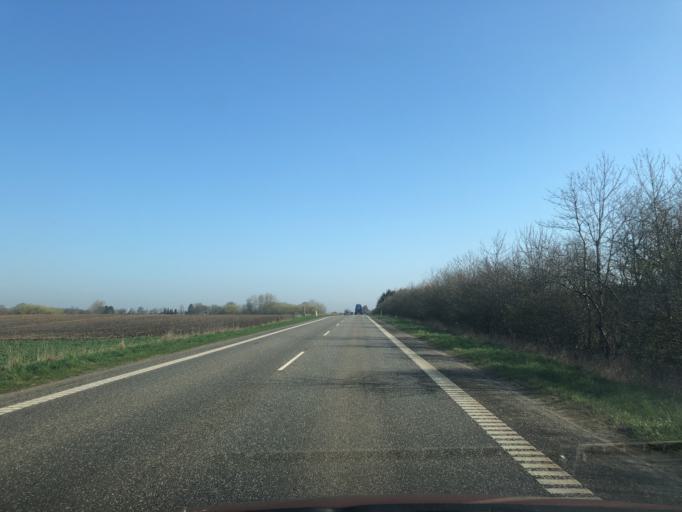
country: DK
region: Zealand
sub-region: Faxe Kommune
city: Ronnede
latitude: 55.2805
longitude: 12.0334
